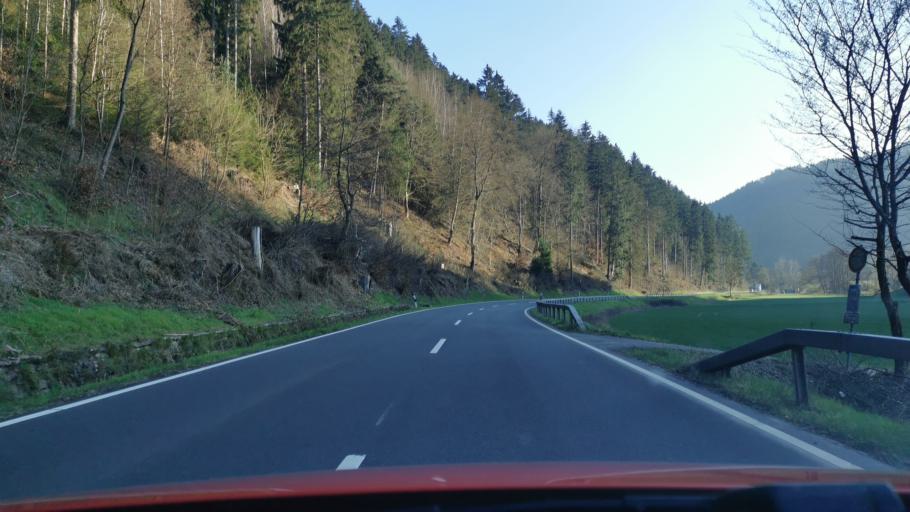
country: DE
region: Rheinland-Pfalz
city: Kordel
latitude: 49.8288
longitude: 6.6535
